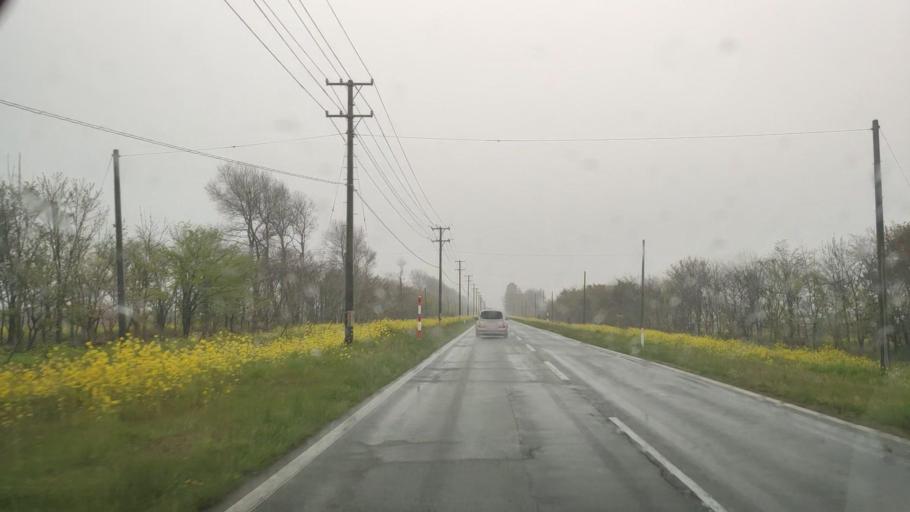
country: JP
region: Akita
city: Tenno
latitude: 39.9800
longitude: 139.9462
